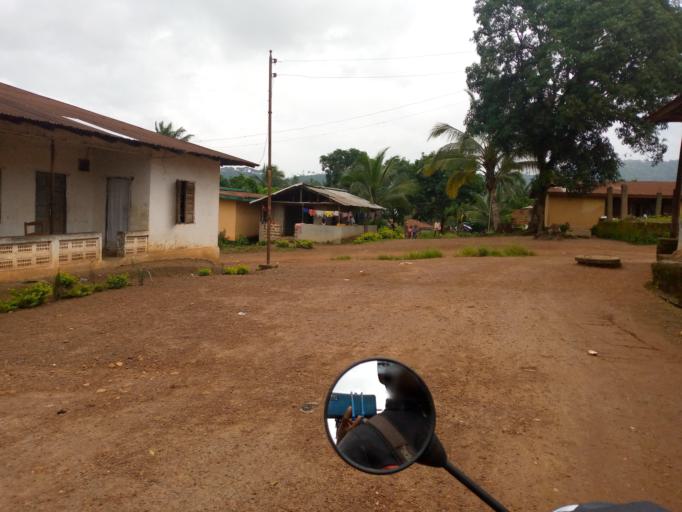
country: SL
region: Eastern Province
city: Kenema
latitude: 7.8647
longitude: -11.1918
